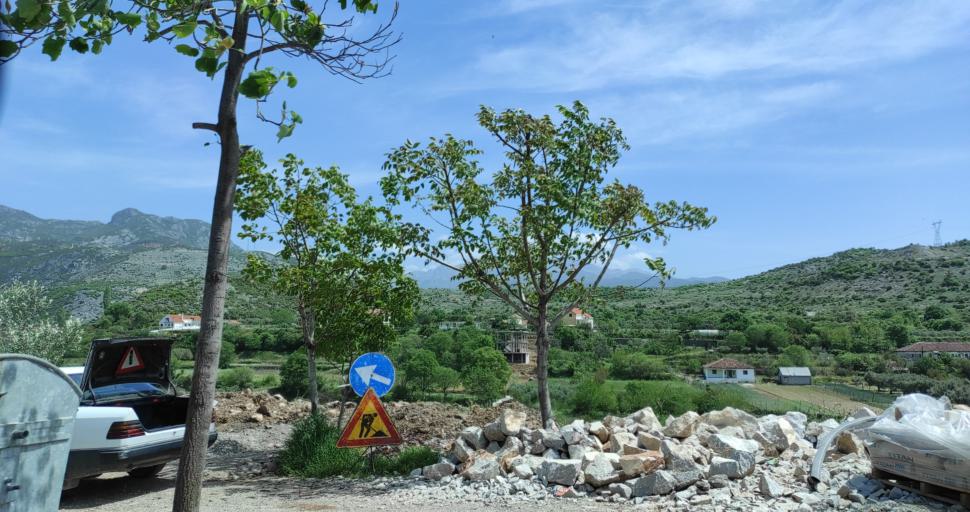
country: AL
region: Shkoder
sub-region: Rrethi i Malesia e Madhe
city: Gruemire
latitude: 42.1199
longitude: 19.5762
